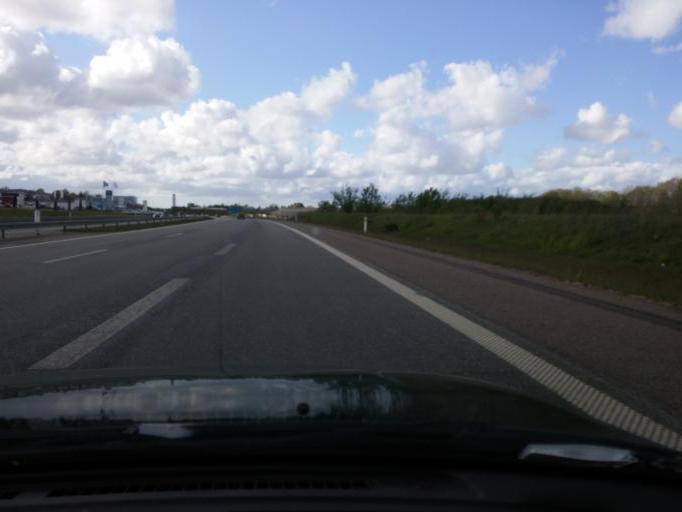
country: DK
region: South Denmark
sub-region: Faaborg-Midtfyn Kommune
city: Ringe
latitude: 55.2406
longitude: 10.4894
